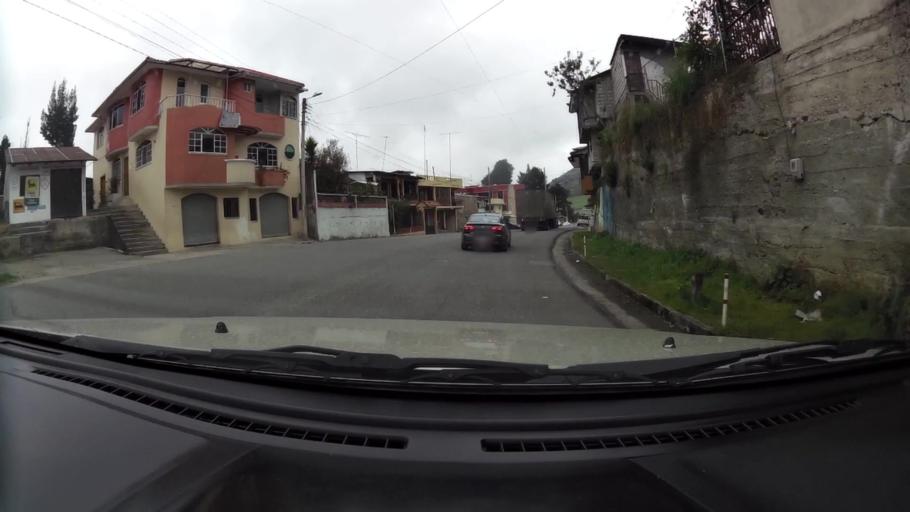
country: EC
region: Canar
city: Canar
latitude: -2.3746
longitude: -78.9705
